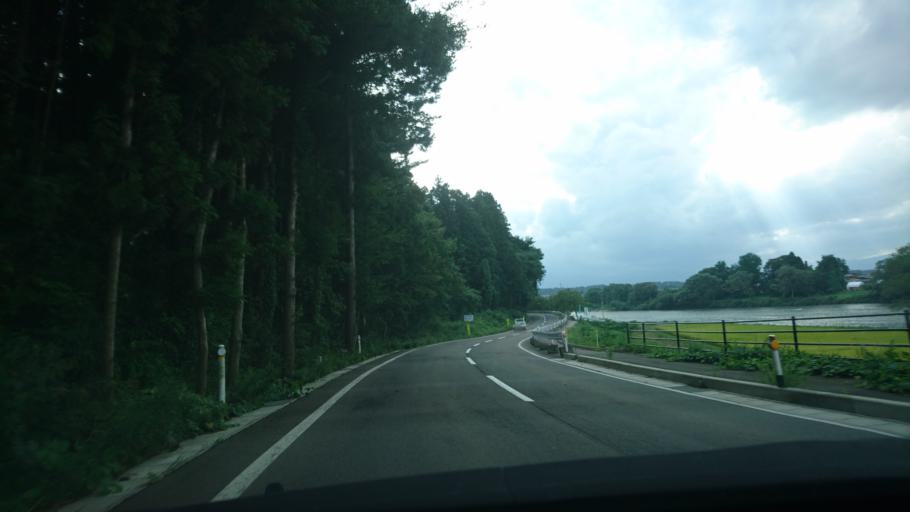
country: JP
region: Iwate
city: Kitakami
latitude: 39.3126
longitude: 141.1566
